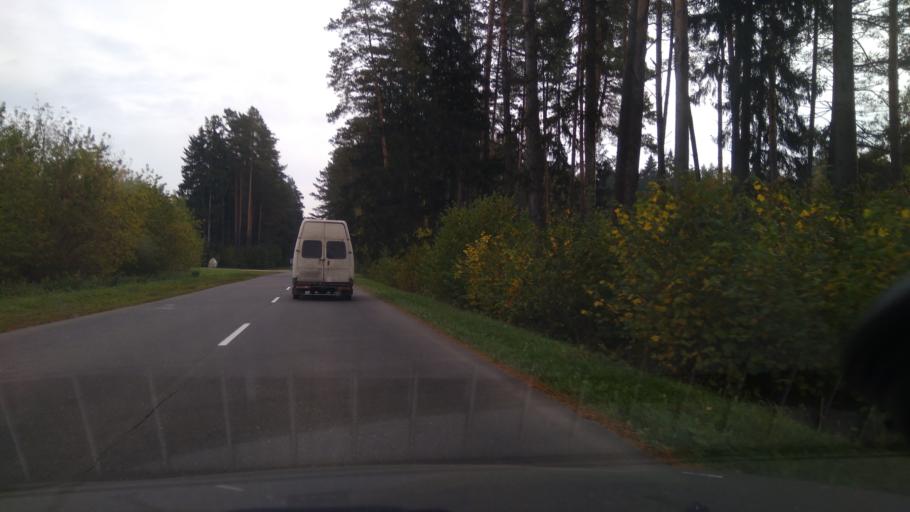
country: BY
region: Minsk
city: Rudzyensk
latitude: 53.6138
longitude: 27.7772
